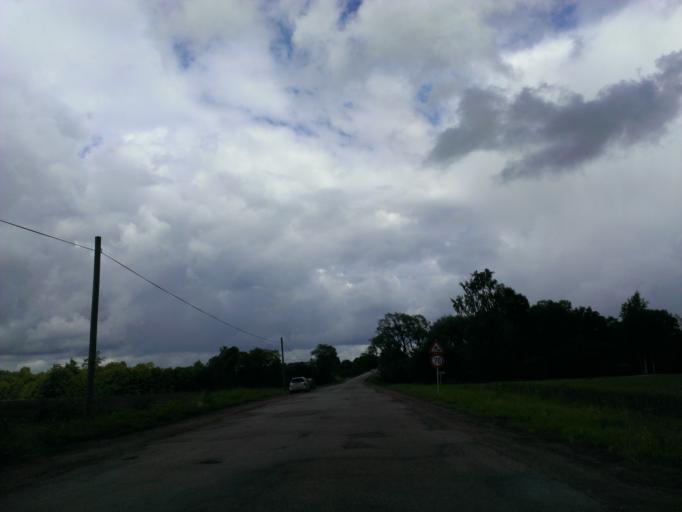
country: LV
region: Sigulda
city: Sigulda
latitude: 57.1641
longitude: 24.9062
